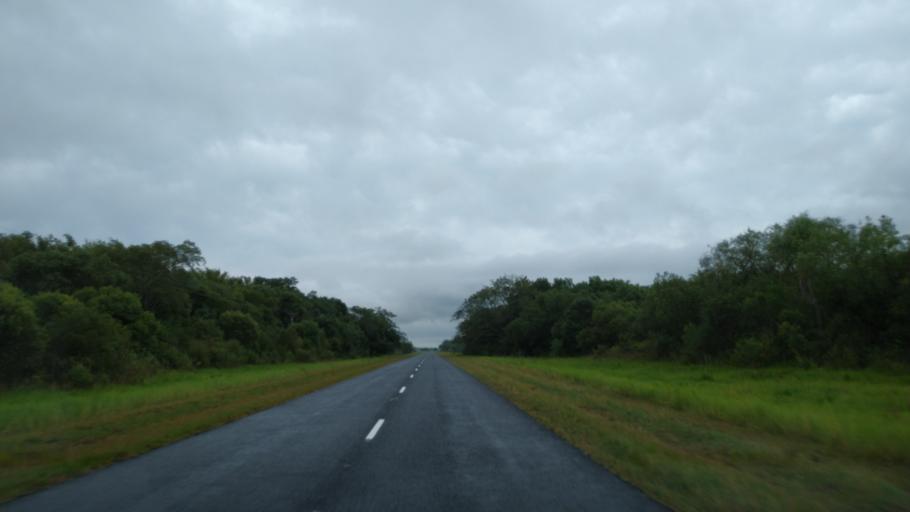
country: AR
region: Corrientes
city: Loreto
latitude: -27.7362
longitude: -57.2456
